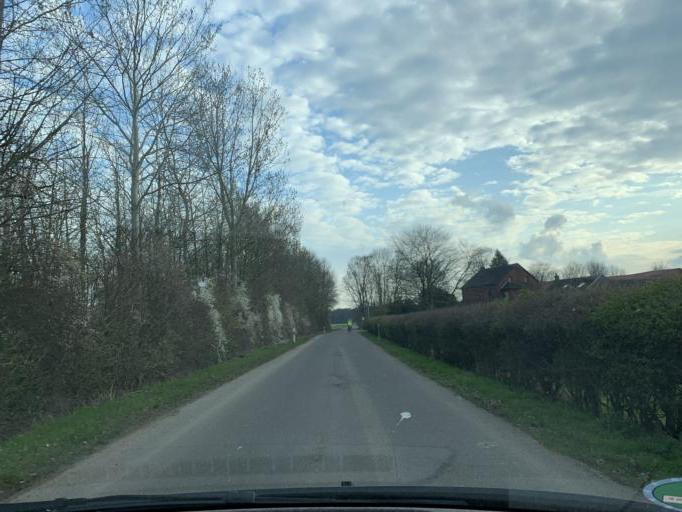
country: DE
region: North Rhine-Westphalia
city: Julich
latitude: 50.9397
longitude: 6.4100
